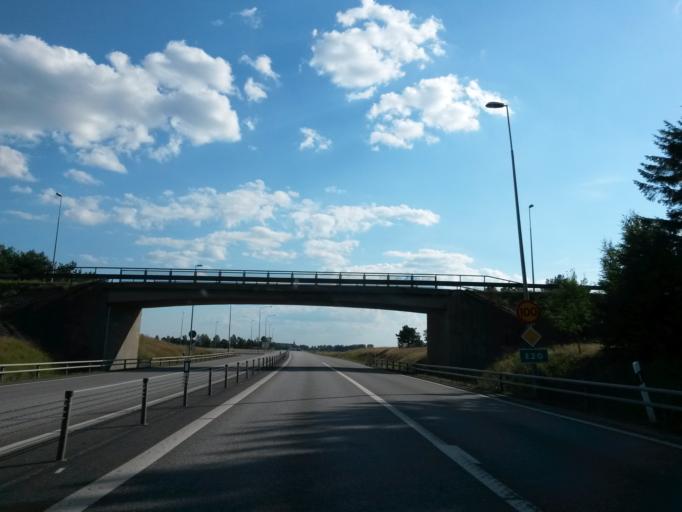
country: SE
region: Vaestra Goetaland
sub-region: Vara Kommun
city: Vara
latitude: 58.2789
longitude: 13.0199
